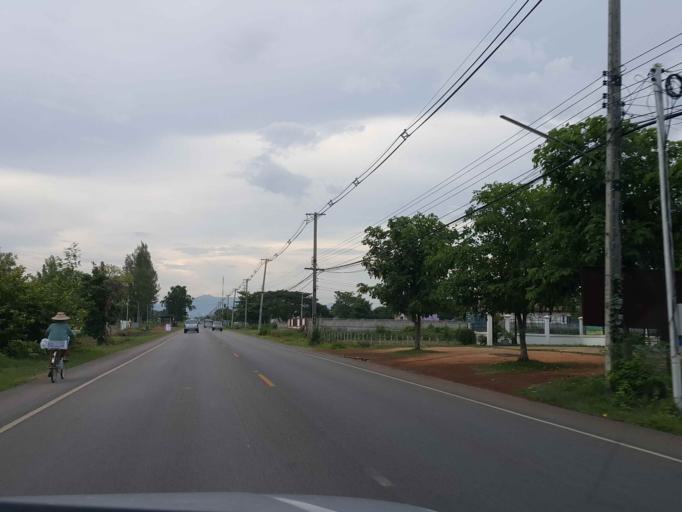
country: TH
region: Lampang
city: Hang Chat
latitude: 18.2727
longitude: 99.3859
